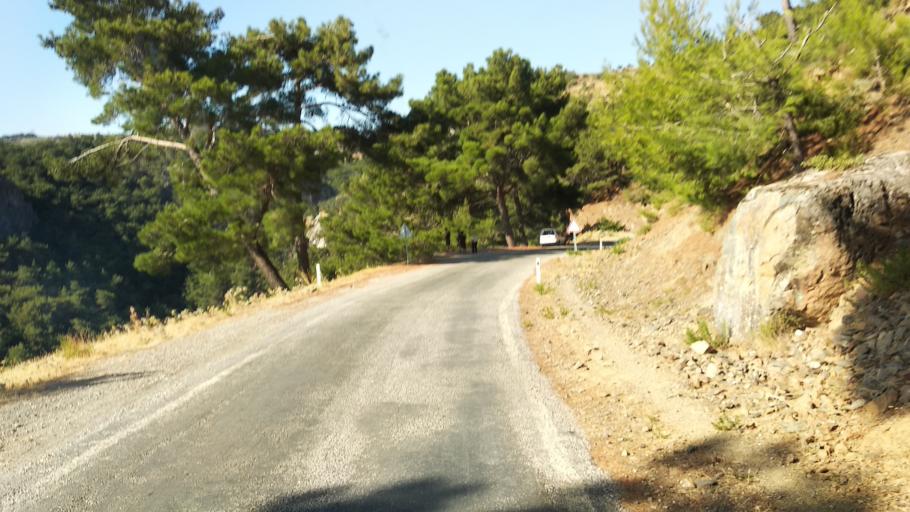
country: TR
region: Izmir
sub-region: Seferihisar
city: Seferhisar
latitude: 38.3162
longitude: 26.9573
